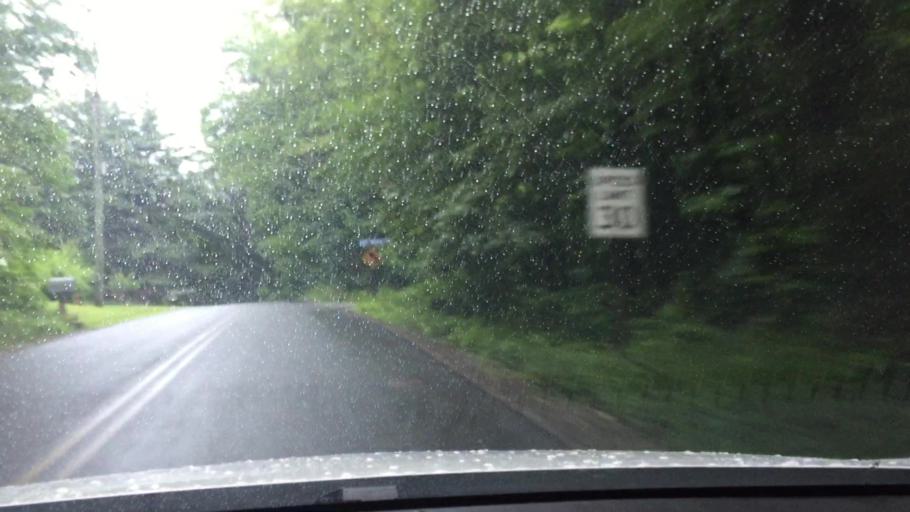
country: US
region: Massachusetts
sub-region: Berkshire County
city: Becket
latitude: 42.2740
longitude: -73.0206
